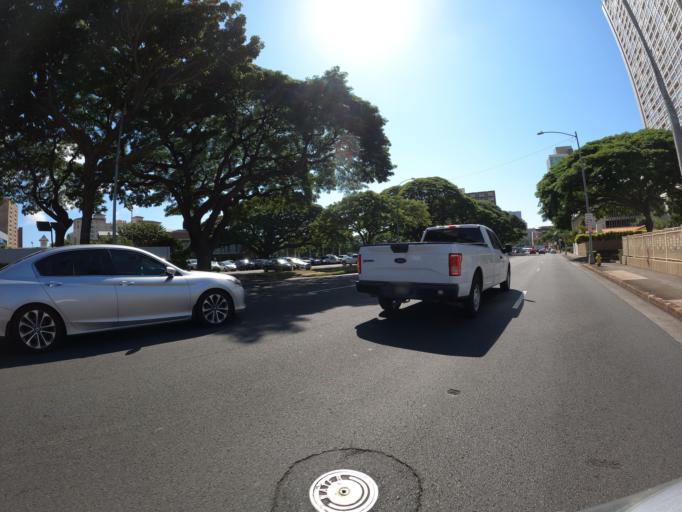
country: US
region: Hawaii
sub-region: Honolulu County
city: Honolulu
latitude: 21.3000
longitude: -157.8345
